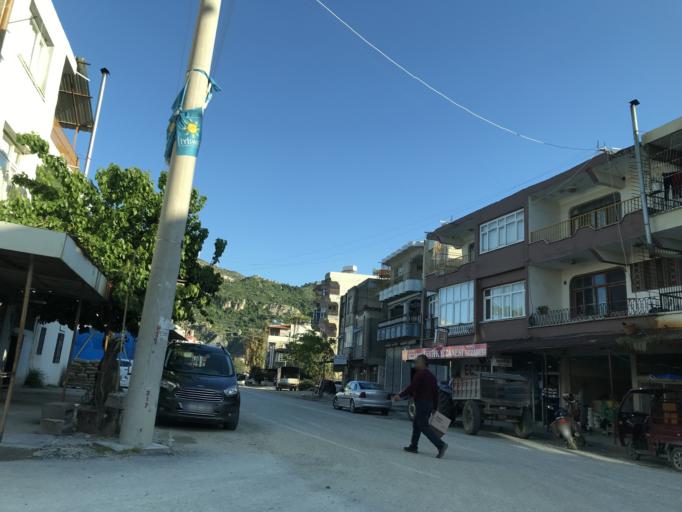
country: TR
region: Hatay
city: Samandag
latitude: 36.0789
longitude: 36.0008
